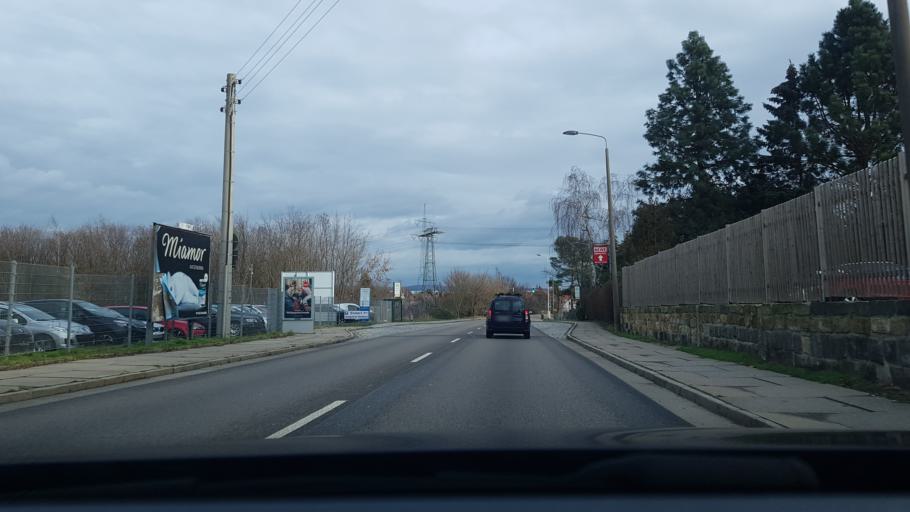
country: DE
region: Saxony
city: Heidenau
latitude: 50.9814
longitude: 13.8444
